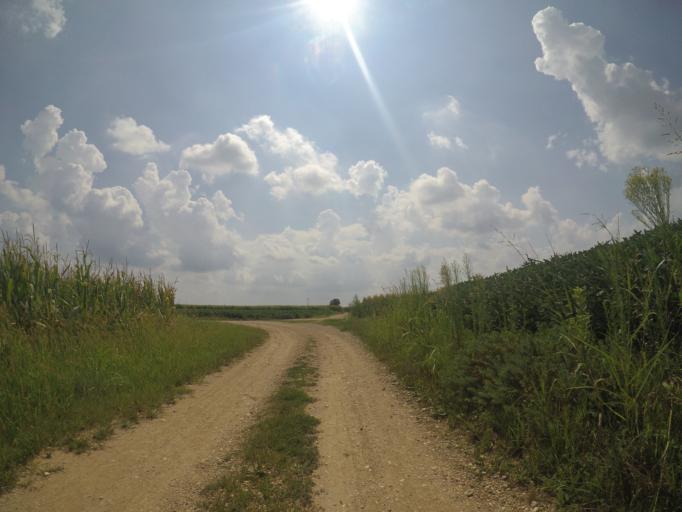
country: IT
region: Friuli Venezia Giulia
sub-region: Provincia di Udine
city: Bertiolo
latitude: 45.9641
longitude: 13.0494
